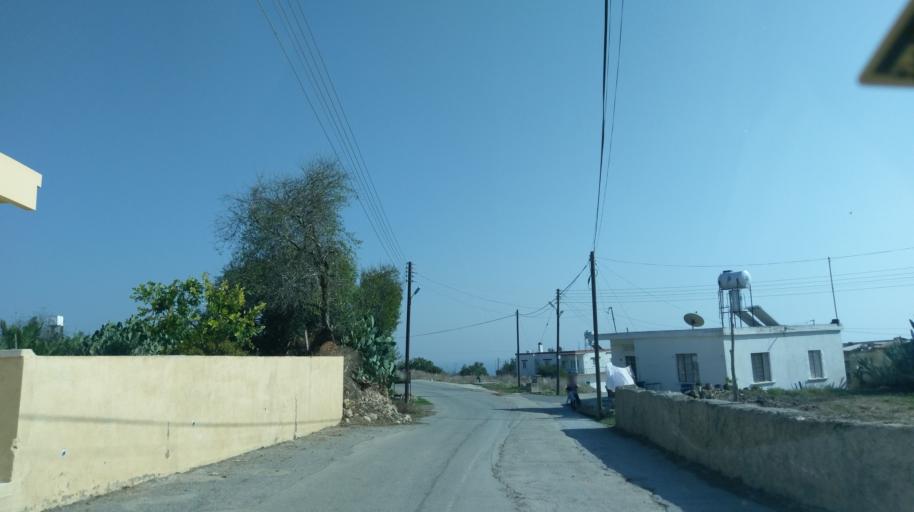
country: CY
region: Ammochostos
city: Leonarisso
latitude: 35.4906
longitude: 34.2189
